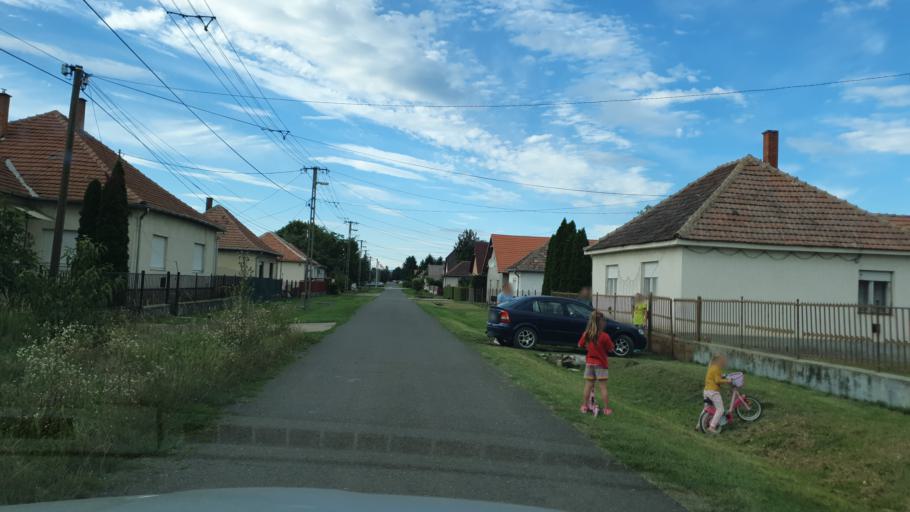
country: HU
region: Heves
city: Zagyvaszanto
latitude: 47.7668
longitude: 19.6678
